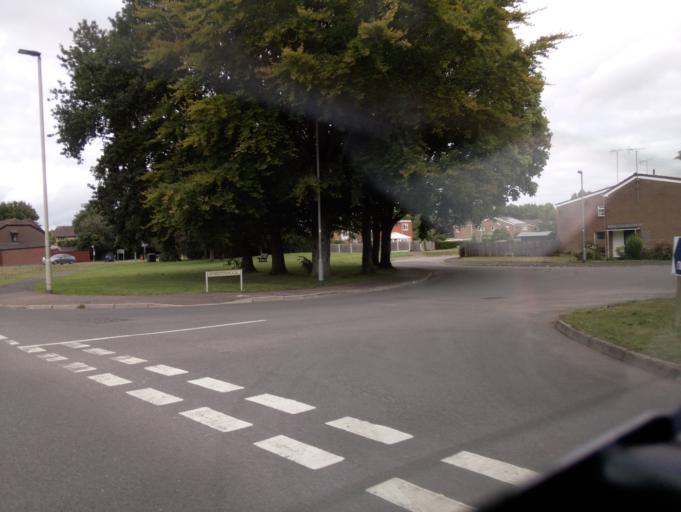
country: GB
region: England
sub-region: Devon
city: Cullompton
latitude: 50.8488
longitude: -3.3947
